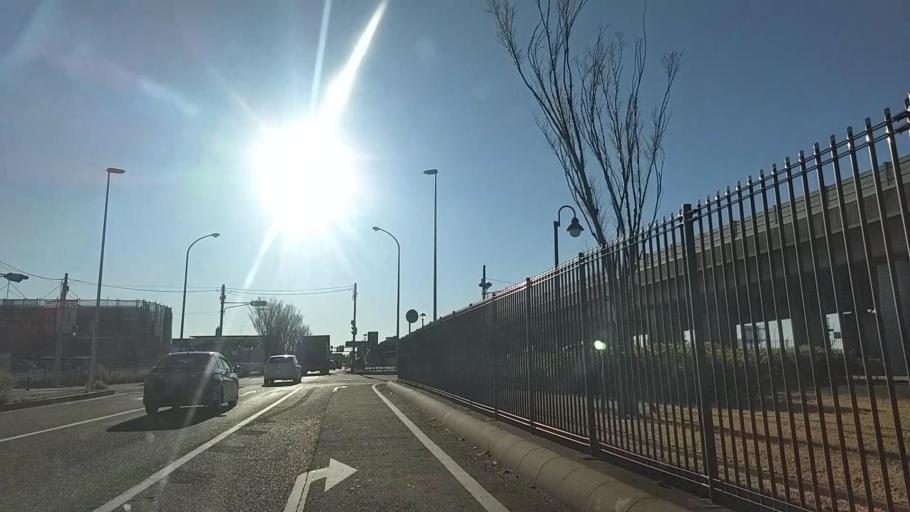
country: JP
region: Chiba
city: Kisarazu
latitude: 35.4322
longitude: 139.9244
